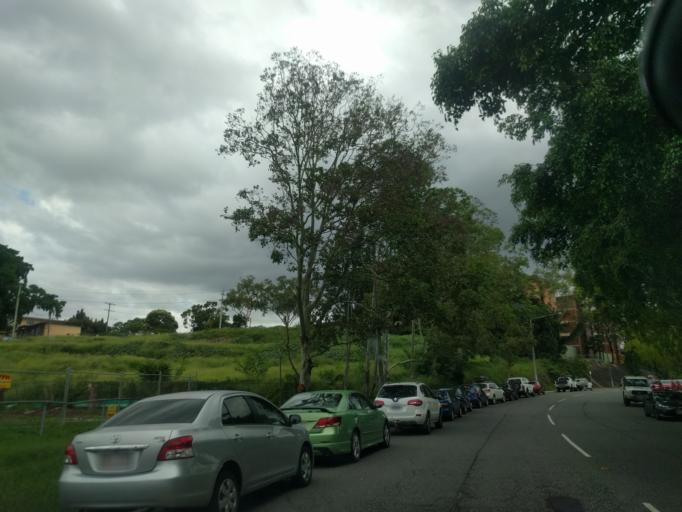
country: AU
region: Queensland
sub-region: Brisbane
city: South Brisbane
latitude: -27.4963
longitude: 153.0067
